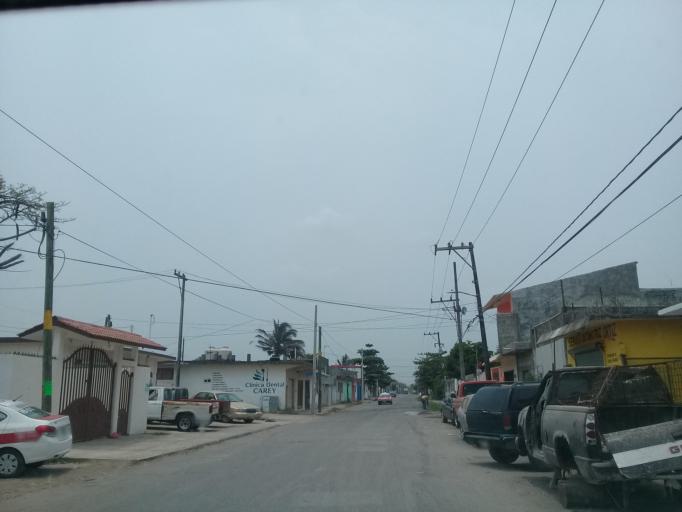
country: MX
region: Veracruz
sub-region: Veracruz
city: Las Amapolas
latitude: 19.1474
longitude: -96.2011
